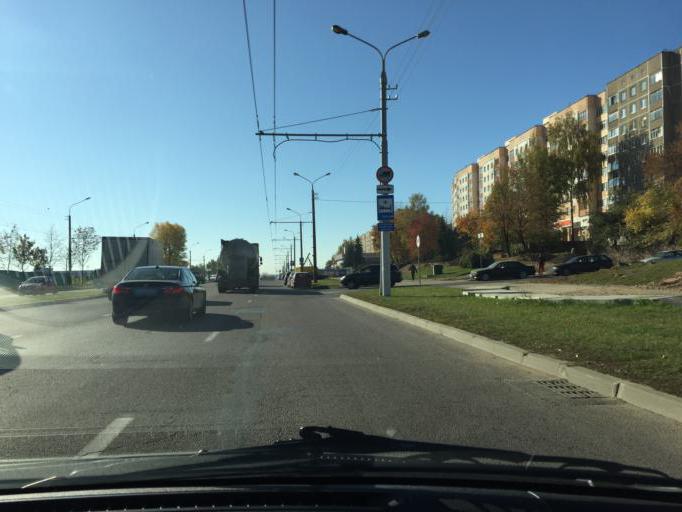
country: BY
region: Minsk
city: Syenitsa
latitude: 53.8489
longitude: 27.5361
